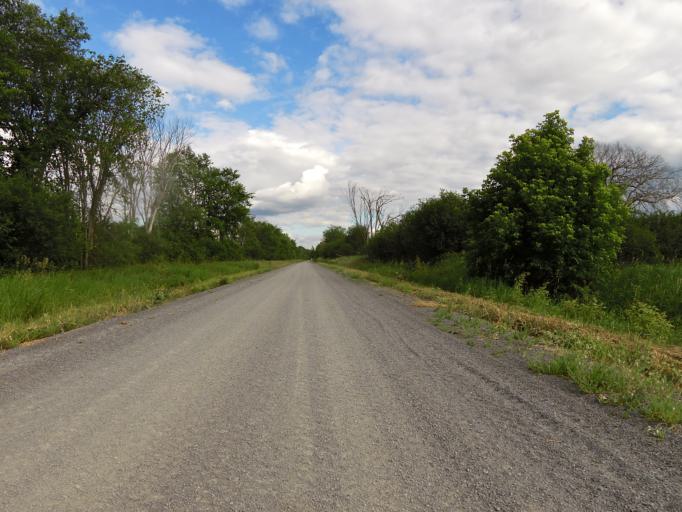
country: CA
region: Ontario
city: Arnprior
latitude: 45.3065
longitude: -76.2735
